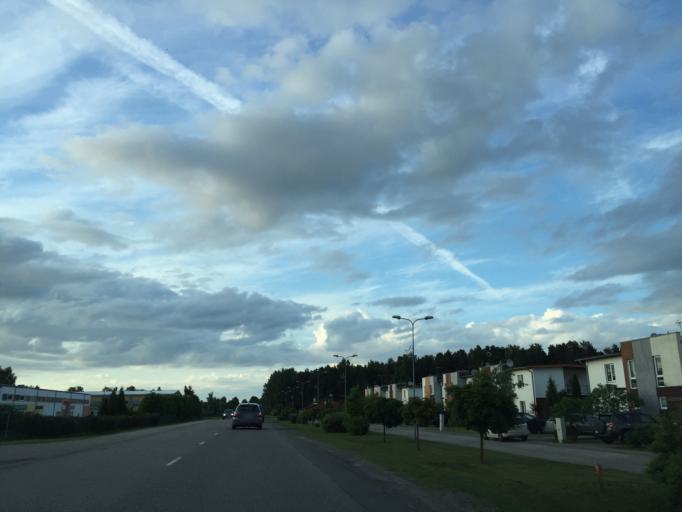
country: LV
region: Babite
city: Pinki
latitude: 56.9481
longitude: 23.9122
